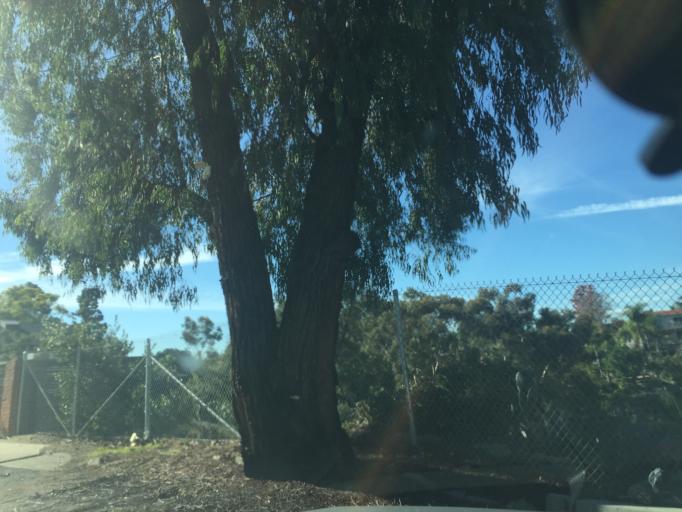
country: US
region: California
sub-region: San Diego County
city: Lemon Grove
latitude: 32.7634
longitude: -117.0919
